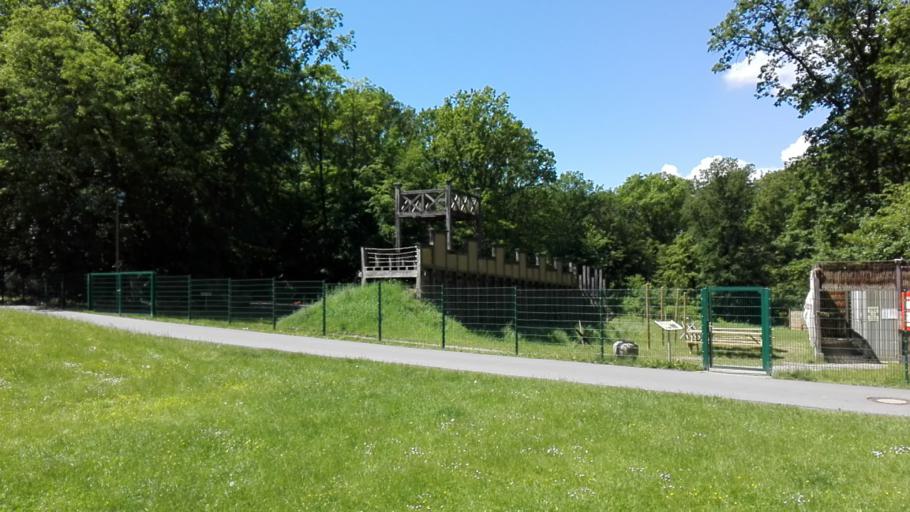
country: DE
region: North Rhine-Westphalia
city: Lanstrop
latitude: 51.6140
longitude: 7.5832
